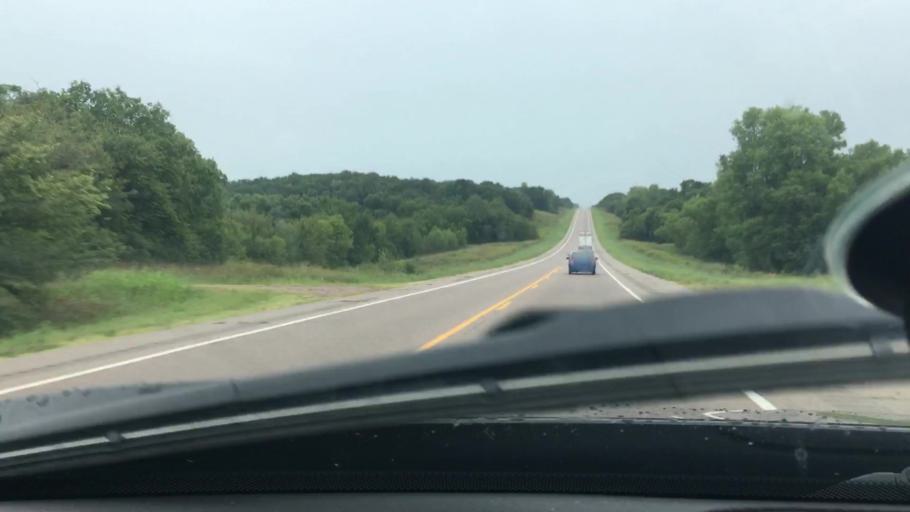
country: US
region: Oklahoma
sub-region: Seminole County
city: Maud
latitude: 35.1126
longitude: -96.6786
